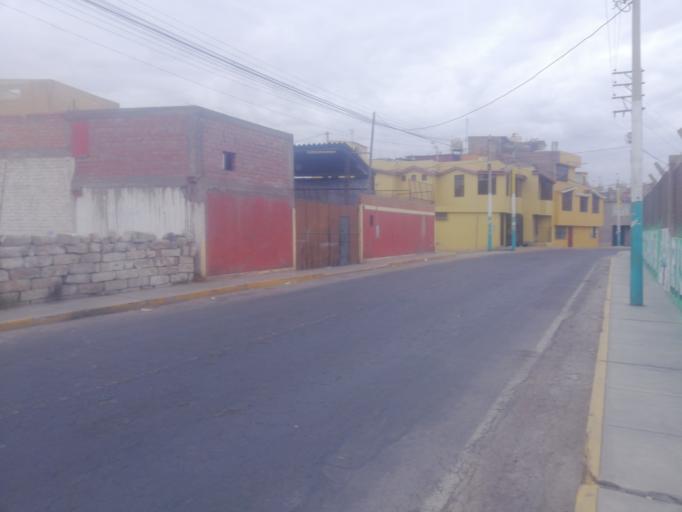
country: PE
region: Arequipa
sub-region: Provincia de Arequipa
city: Tiabaya
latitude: -16.4468
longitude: -71.5884
